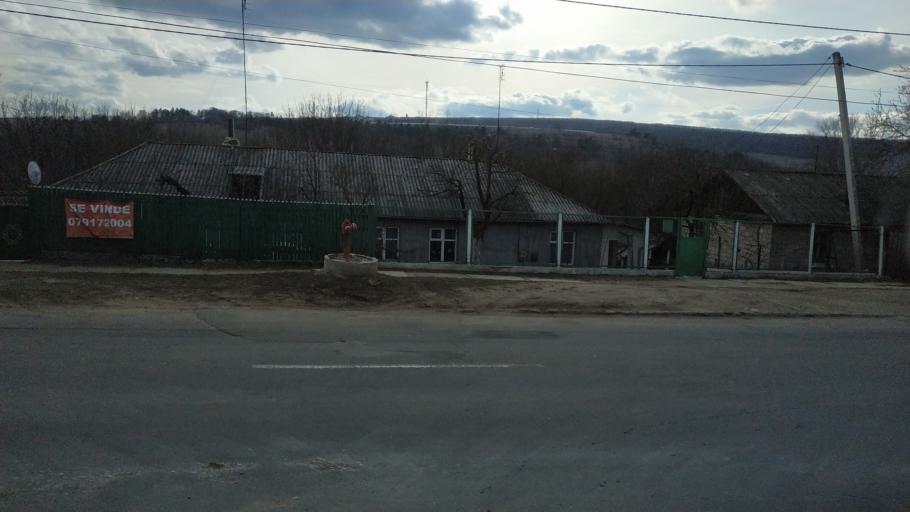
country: MD
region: Hincesti
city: Hincesti
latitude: 46.8344
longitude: 28.5785
